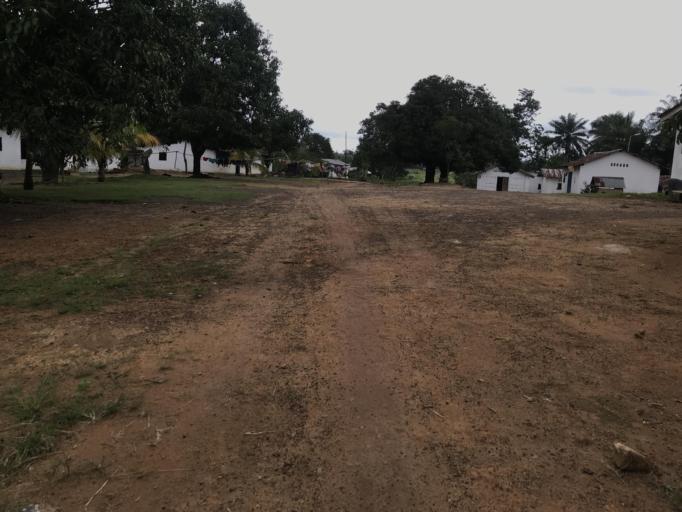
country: GN
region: Nzerekore
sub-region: Prefecture de Guekedou
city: Gueckedou
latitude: 8.4726
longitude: -10.2831
